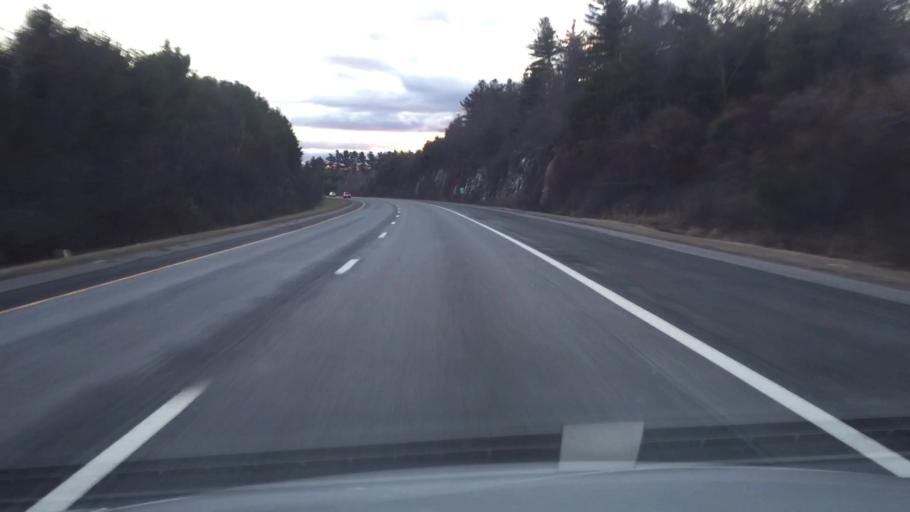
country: US
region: Massachusetts
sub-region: Worcester County
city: West Boylston
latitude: 42.3945
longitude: -71.8129
